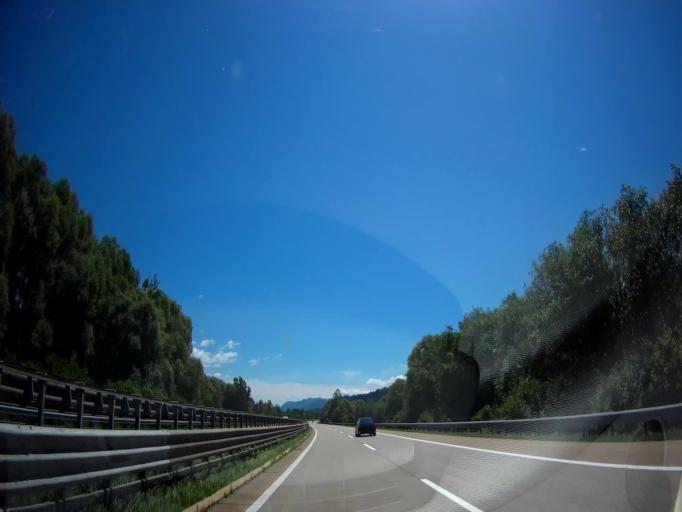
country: AT
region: Carinthia
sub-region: Politischer Bezirk Spittal an der Drau
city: Millstatt
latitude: 46.7559
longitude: 13.5679
